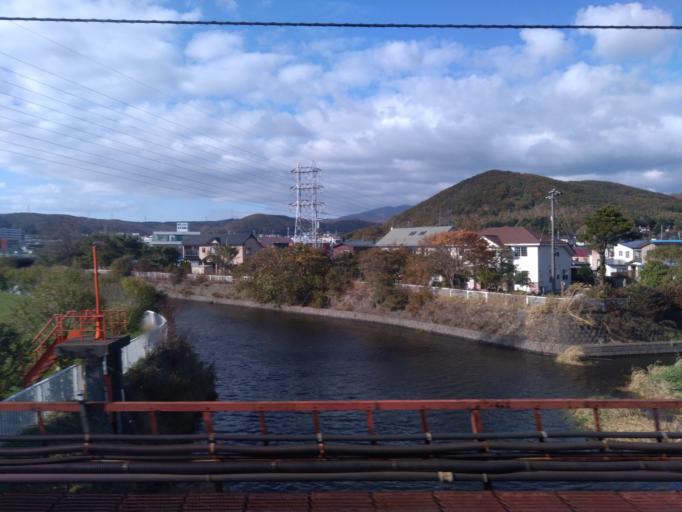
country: JP
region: Hokkaido
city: Muroran
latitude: 42.3614
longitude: 141.0467
